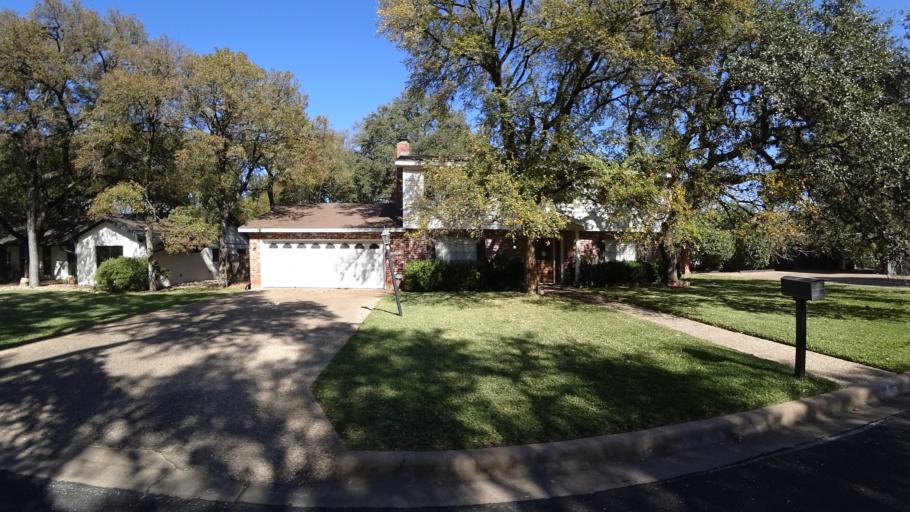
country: US
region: Texas
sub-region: Williamson County
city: Jollyville
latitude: 30.3791
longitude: -97.7509
